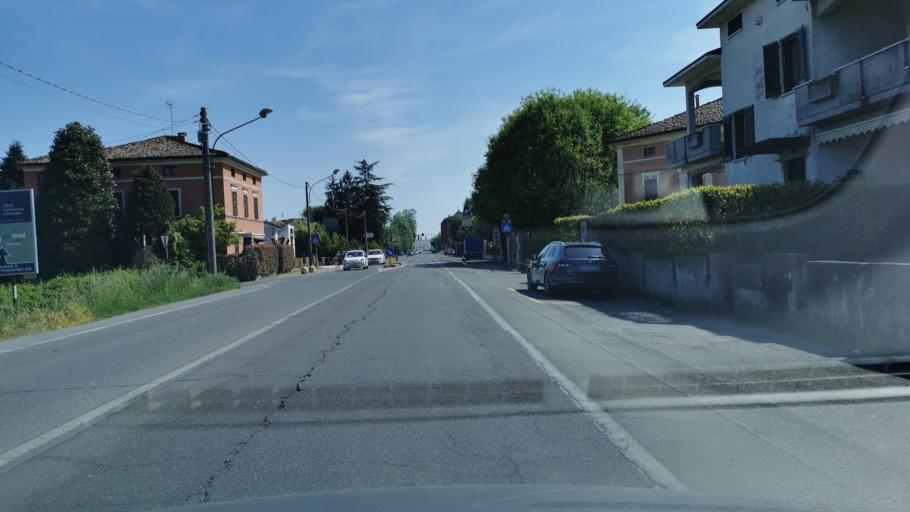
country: IT
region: Emilia-Romagna
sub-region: Provincia di Piacenza
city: Castelvetro Piacentino
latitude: 45.1164
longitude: 9.9923
